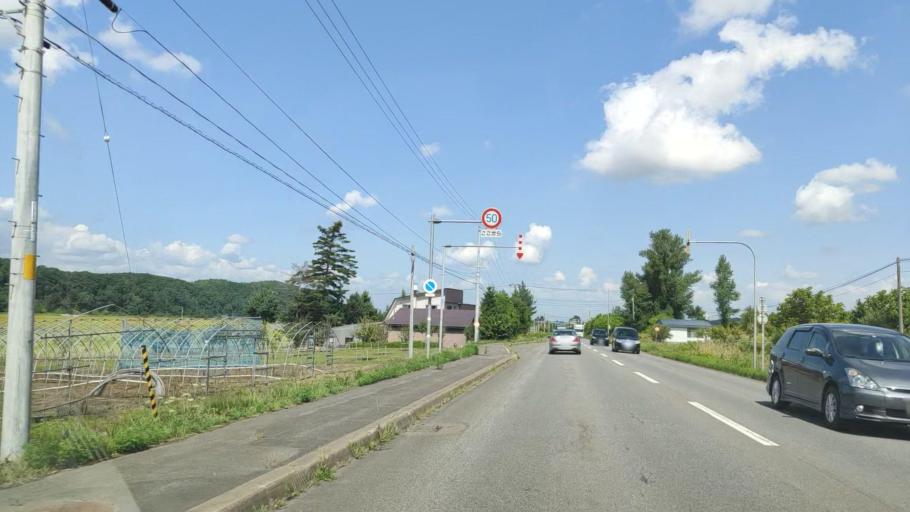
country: JP
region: Hokkaido
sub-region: Asahikawa-shi
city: Asahikawa
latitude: 43.6355
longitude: 142.4562
